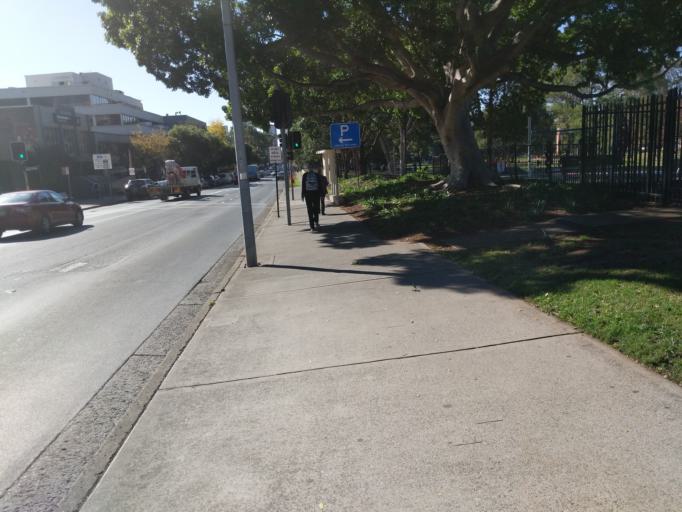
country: AU
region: New South Wales
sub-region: Fairfield
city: Liverpool
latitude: -33.9226
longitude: 150.9270
